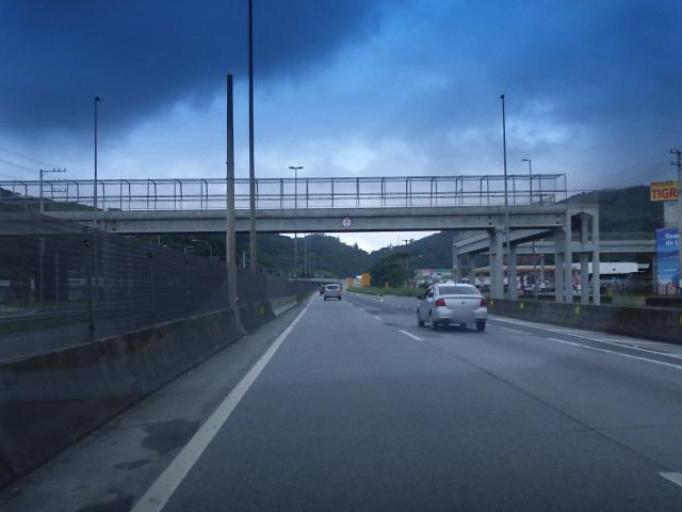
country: BR
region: Santa Catarina
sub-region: Balneario Camboriu
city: Balneario Camboriu
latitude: -27.0237
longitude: -48.6077
